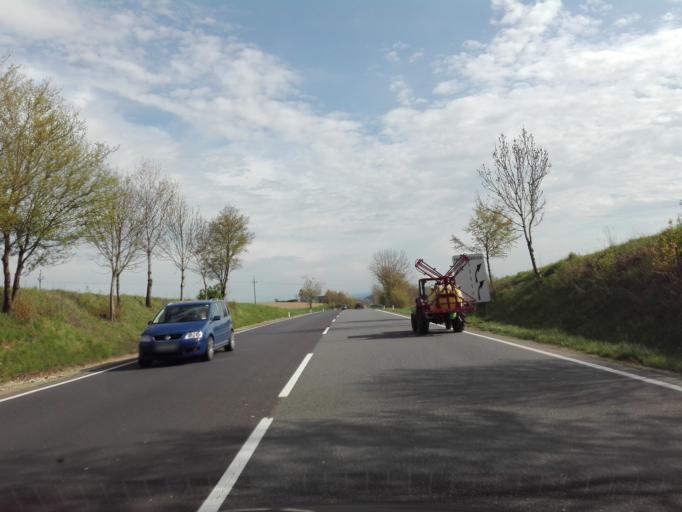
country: AT
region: Upper Austria
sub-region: Politischer Bezirk Urfahr-Umgebung
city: Herzogsdorf
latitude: 48.4148
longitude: 14.0632
